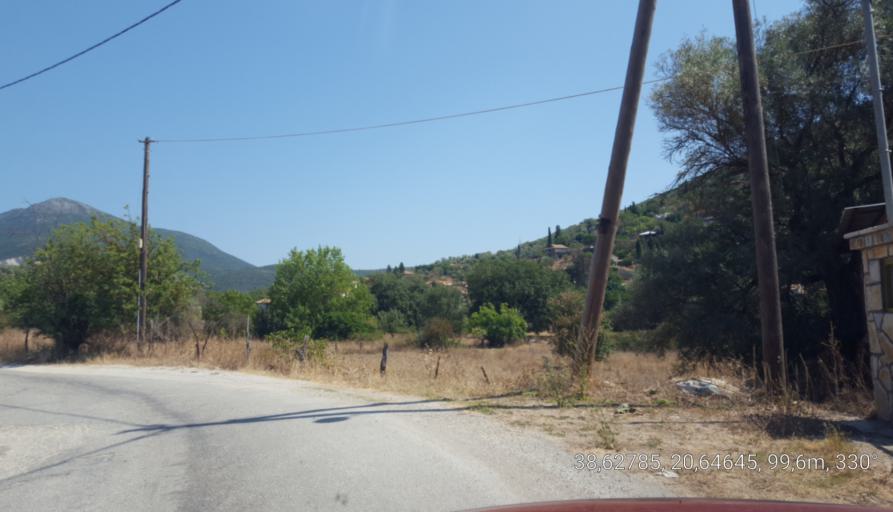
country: GR
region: Ionian Islands
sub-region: Lefkada
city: Nidri
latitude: 38.6278
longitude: 20.6464
